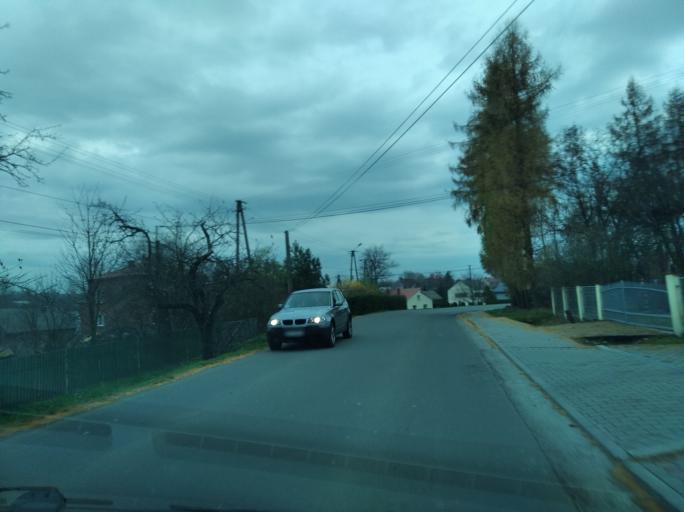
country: PL
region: Subcarpathian Voivodeship
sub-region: Powiat ropczycko-sedziszowski
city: Iwierzyce
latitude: 50.0306
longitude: 21.7543
